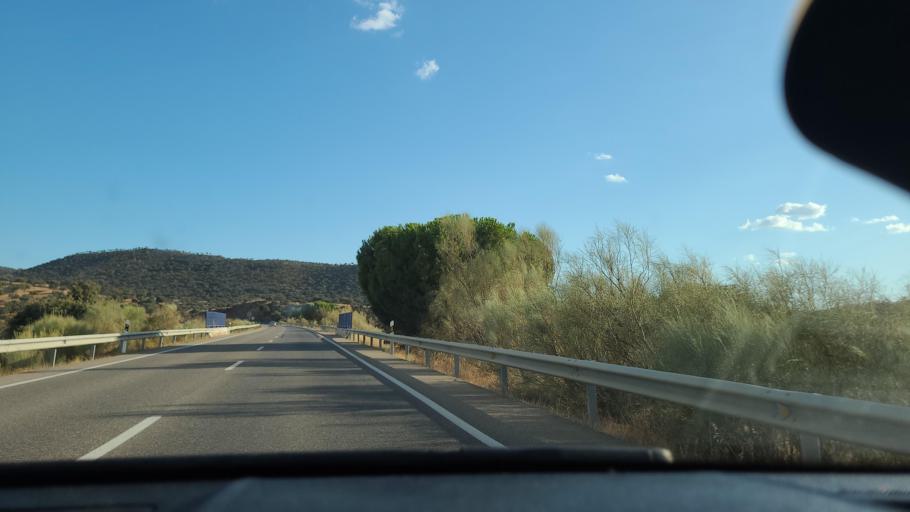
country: ES
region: Andalusia
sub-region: Province of Cordoba
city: Belmez
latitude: 38.2369
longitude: -5.1679
